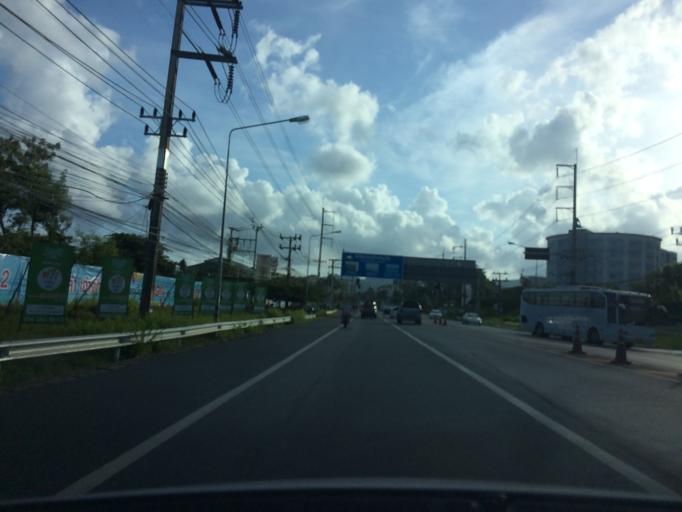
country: TH
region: Phuket
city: Mueang Phuket
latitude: 7.8723
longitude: 98.3625
